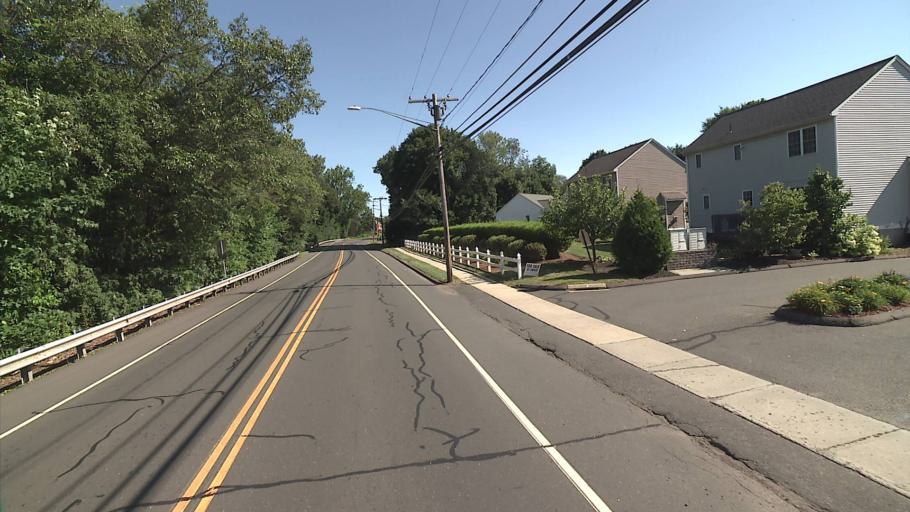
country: US
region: Connecticut
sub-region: New Haven County
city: Cheshire Village
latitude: 41.5751
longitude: -72.8955
